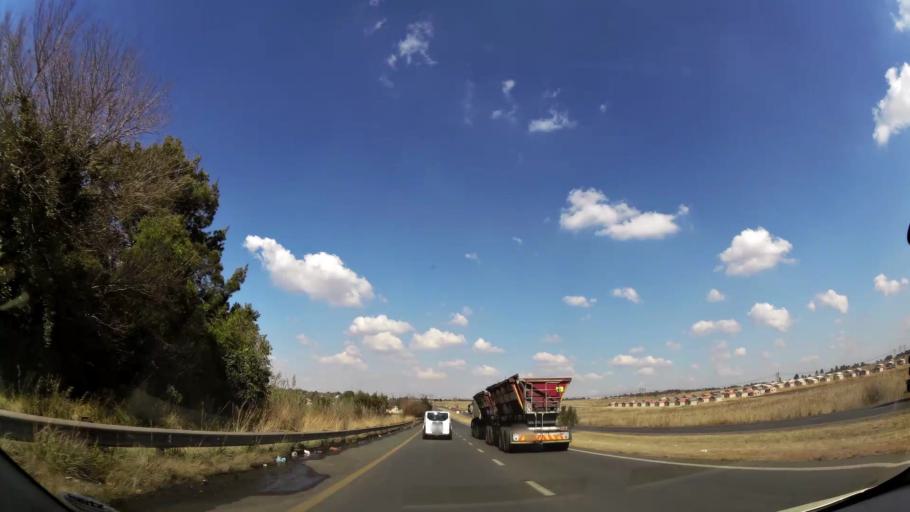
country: ZA
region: Mpumalanga
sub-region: Nkangala District Municipality
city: Witbank
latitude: -25.9301
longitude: 29.2363
